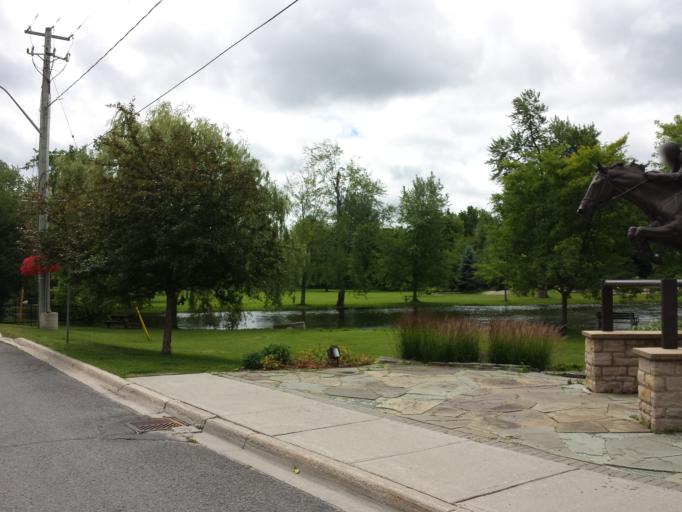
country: CA
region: Ontario
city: Perth
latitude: 44.8996
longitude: -76.2516
